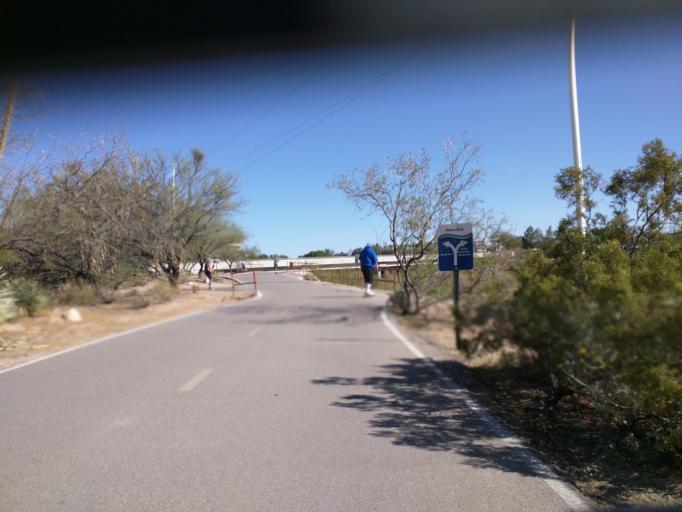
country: US
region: Arizona
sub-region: Pima County
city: Flowing Wells
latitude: 32.2908
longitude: -110.9712
